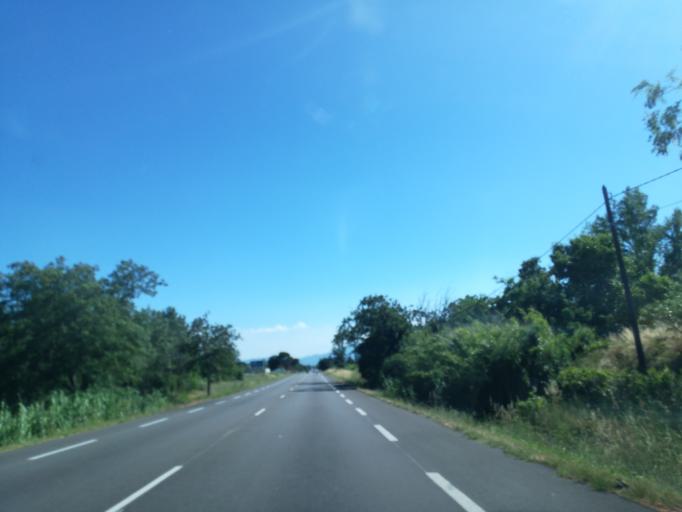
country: FR
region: Languedoc-Roussillon
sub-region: Departement des Pyrenees-Orientales
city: Pollestres
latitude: 42.6246
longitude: 2.8681
